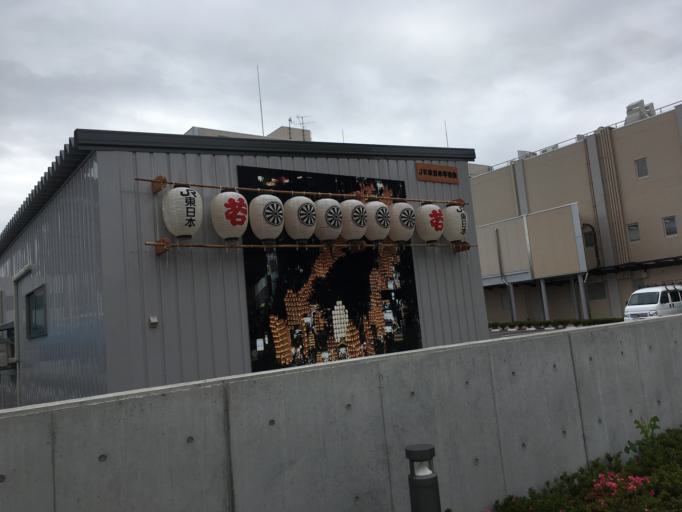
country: JP
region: Akita
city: Akita
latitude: 39.7153
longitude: 140.1284
